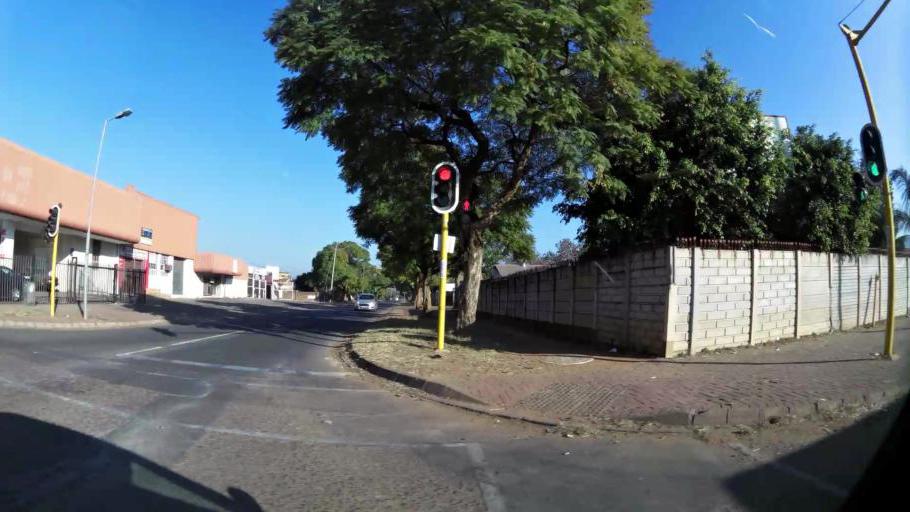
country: ZA
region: Gauteng
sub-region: City of Tshwane Metropolitan Municipality
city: Pretoria
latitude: -25.7125
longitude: 28.1845
